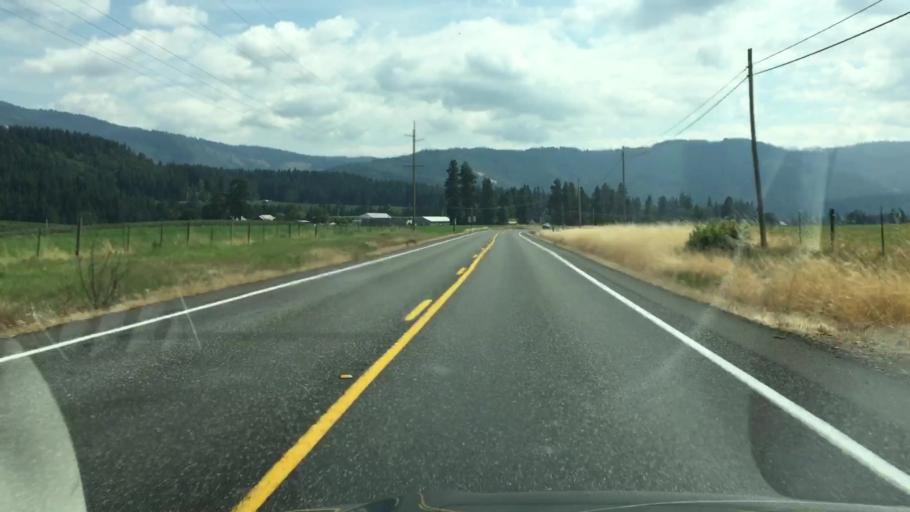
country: US
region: Washington
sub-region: Klickitat County
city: White Salmon
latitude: 45.8226
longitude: -121.4892
